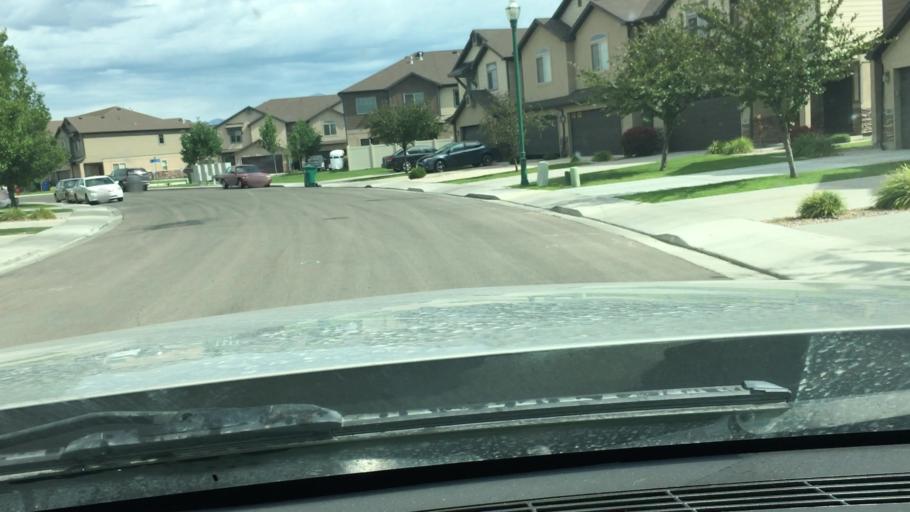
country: US
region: Utah
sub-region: Utah County
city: Orem
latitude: 40.2822
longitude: -111.7394
